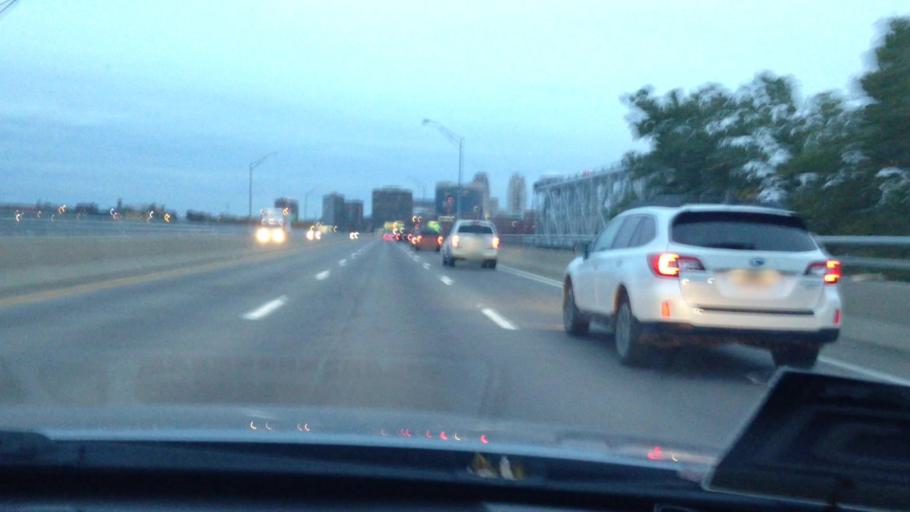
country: US
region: Missouri
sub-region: Jackson County
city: Kansas City
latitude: 39.1182
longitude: -94.5788
